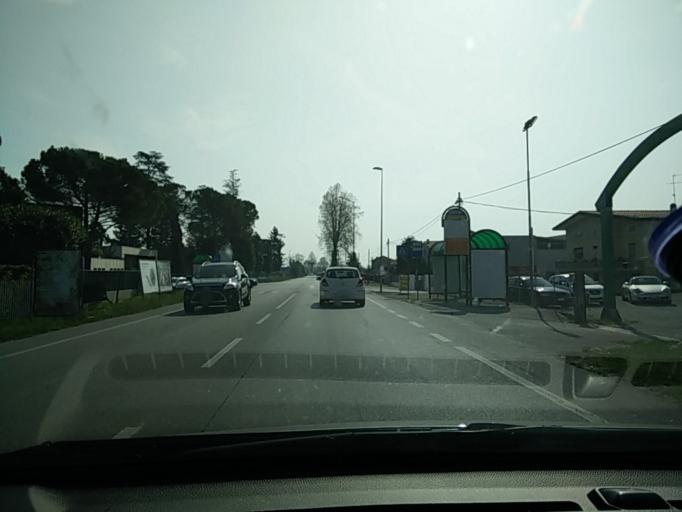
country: IT
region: Friuli Venezia Giulia
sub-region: Provincia di Pordenone
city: Pordenone
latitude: 45.9477
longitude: 12.6840
